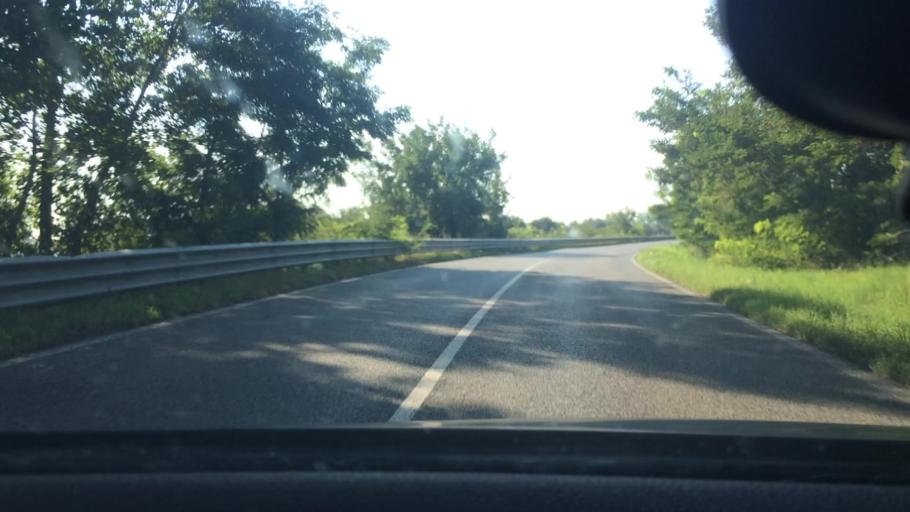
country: IT
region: Emilia-Romagna
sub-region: Provincia di Ferrara
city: Lagosanto
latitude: 44.7451
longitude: 12.1410
